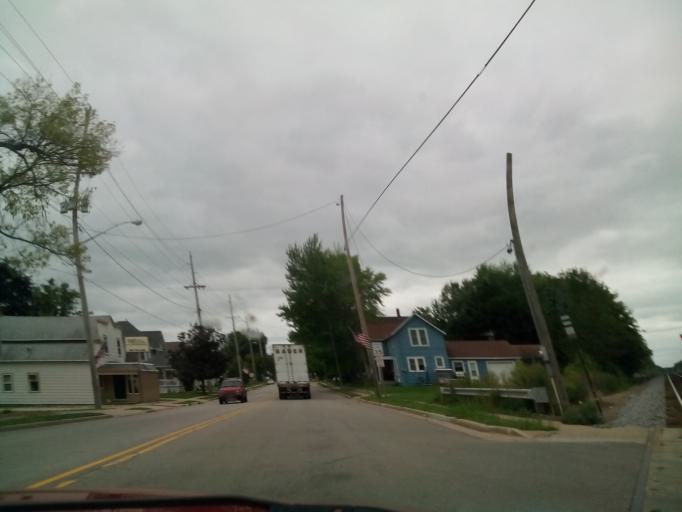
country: US
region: Wisconsin
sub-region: Outagamie County
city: Hortonville
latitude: 44.2730
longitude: -88.6805
